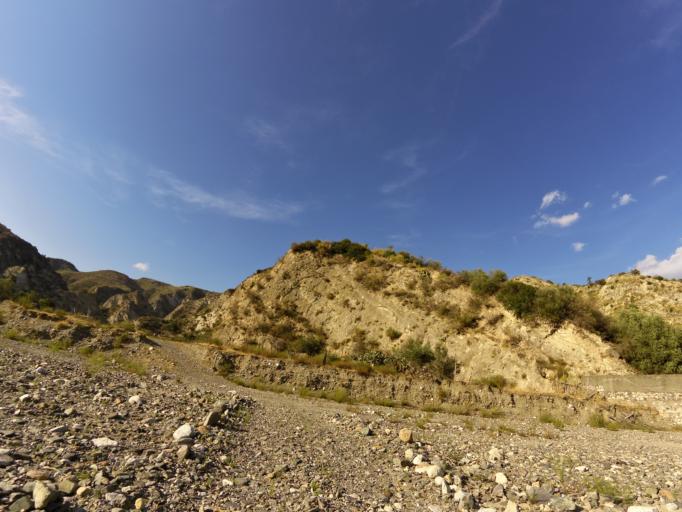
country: IT
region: Calabria
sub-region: Provincia di Reggio Calabria
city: Stilo
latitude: 38.4823
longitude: 16.4780
